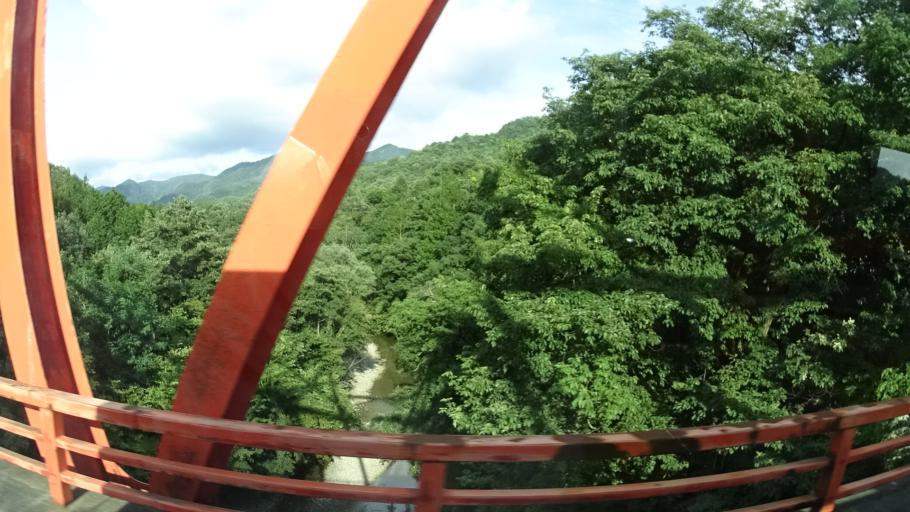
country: JP
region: Tochigi
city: Nikko
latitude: 36.6612
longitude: 139.4595
